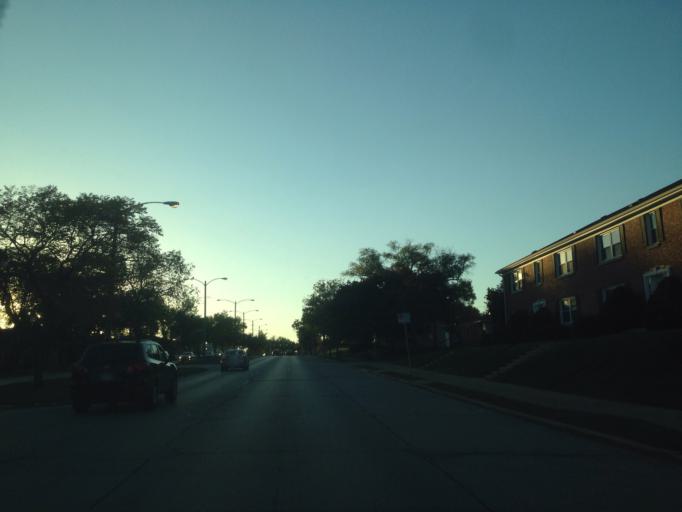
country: US
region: Wisconsin
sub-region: Milwaukee County
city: Wauwatosa
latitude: 43.0360
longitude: -88.0239
